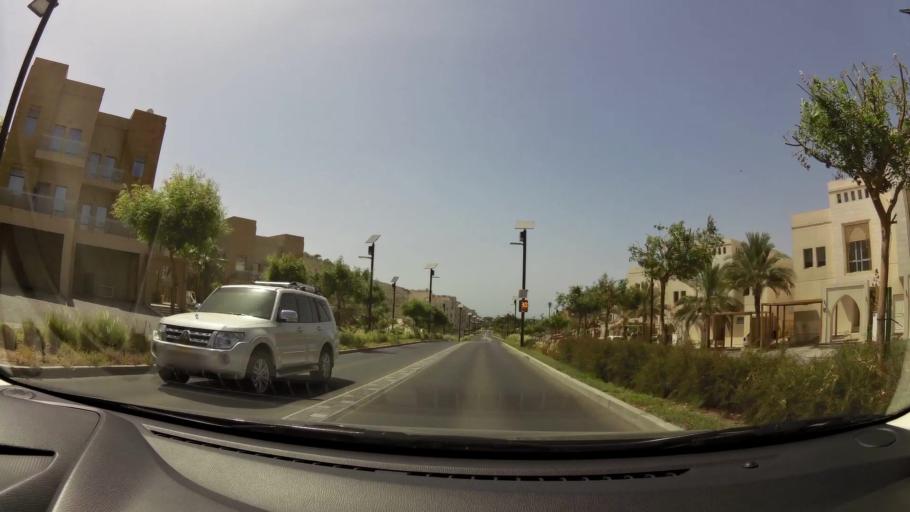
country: OM
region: Muhafazat Masqat
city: Muscat
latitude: 23.6312
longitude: 58.5019
